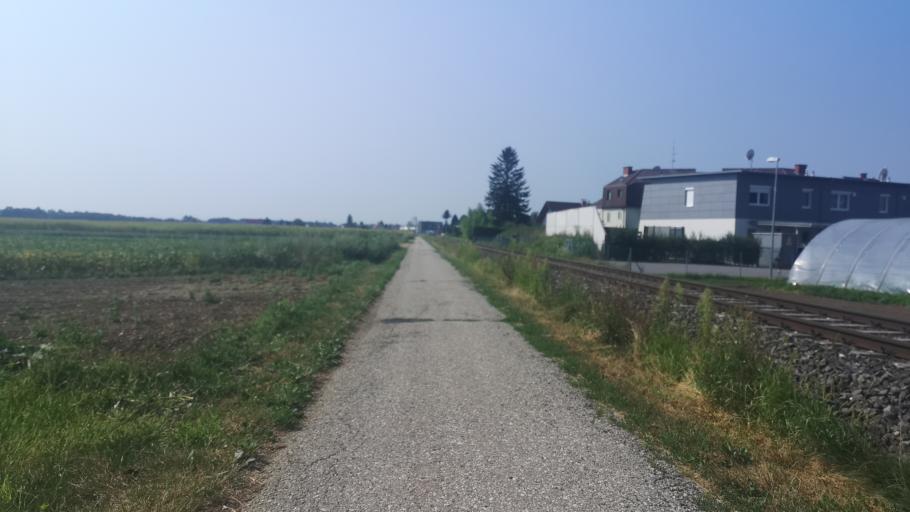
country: AT
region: Styria
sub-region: Politischer Bezirk Graz-Umgebung
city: Seiersberg
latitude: 47.0056
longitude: 15.4016
